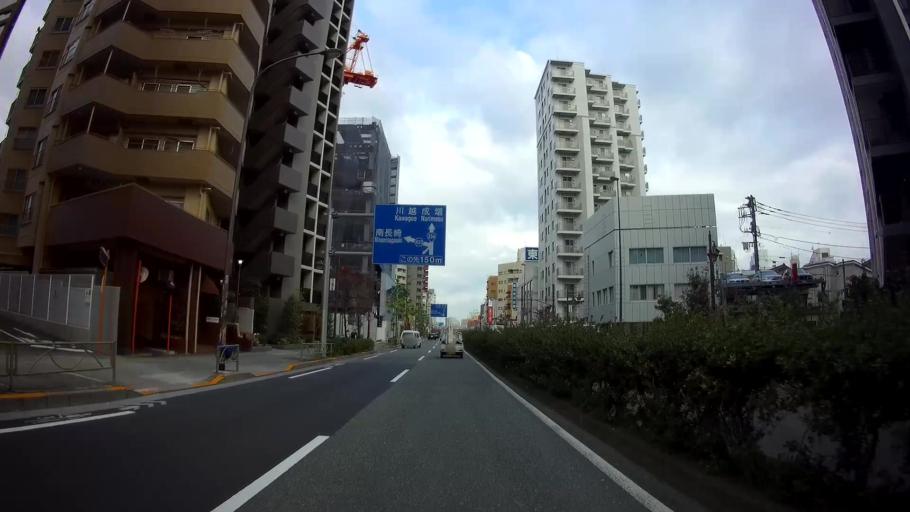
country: JP
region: Tokyo
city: Tokyo
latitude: 35.7470
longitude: 139.6993
